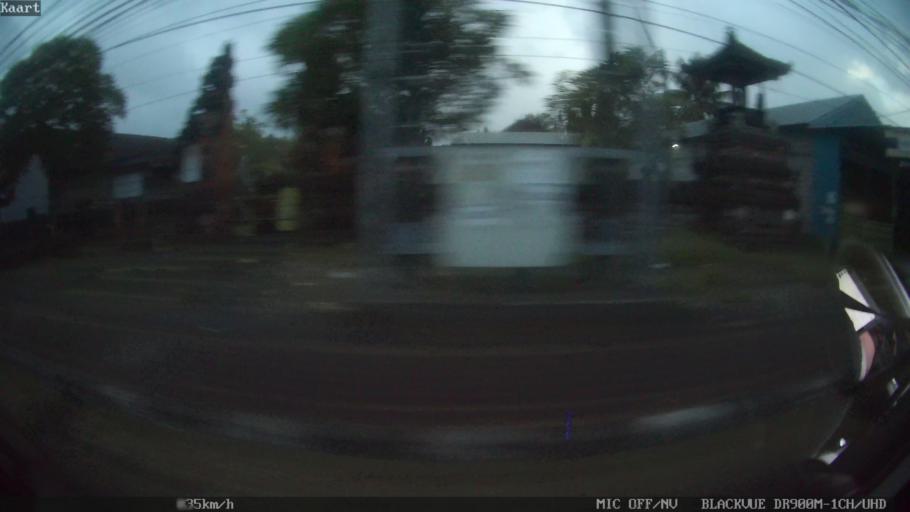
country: ID
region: Bali
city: Banjar Parekan
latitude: -8.5699
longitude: 115.2195
